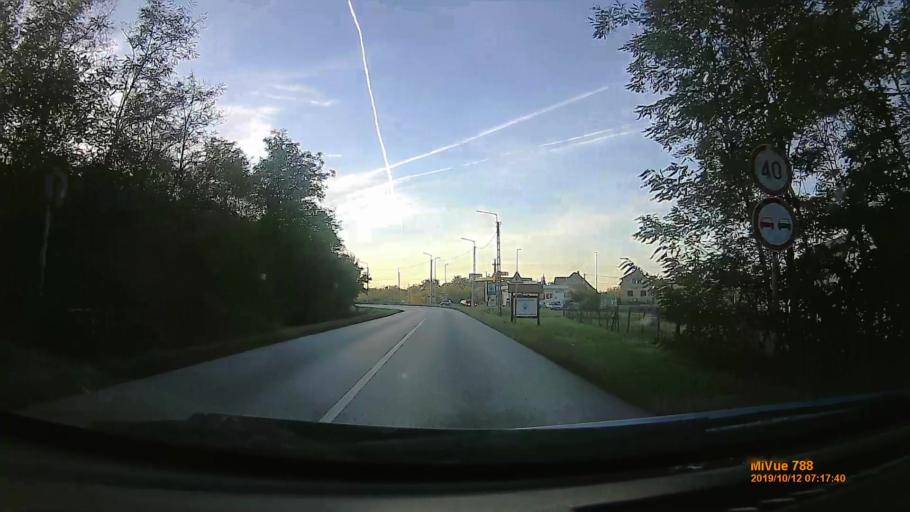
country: HU
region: Hajdu-Bihar
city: Hosszupalyi
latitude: 47.4015
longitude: 21.7226
